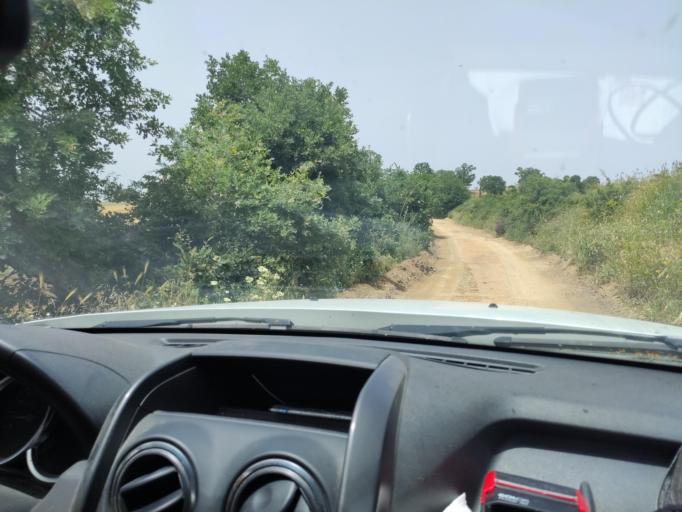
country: MK
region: Radovis
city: Radovish
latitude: 41.6757
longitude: 22.4026
